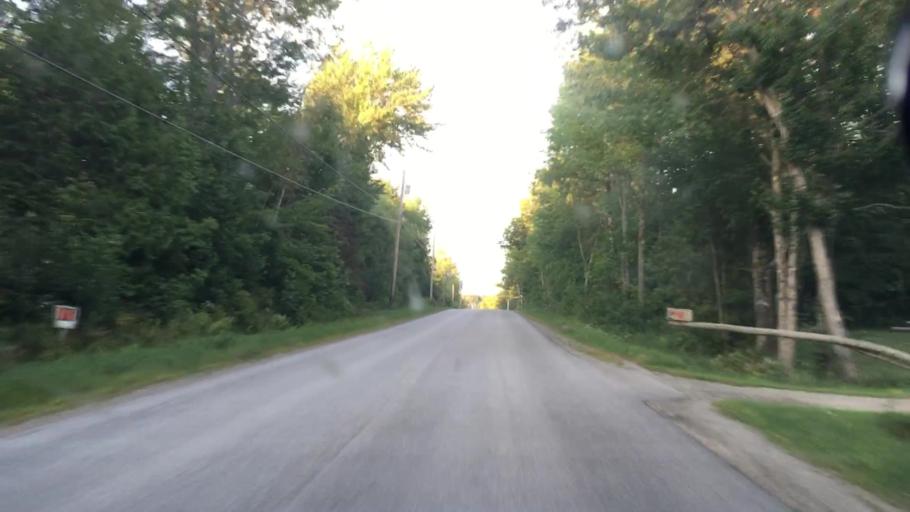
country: US
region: Maine
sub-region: Waldo County
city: Frankfort
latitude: 44.6723
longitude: -68.9254
